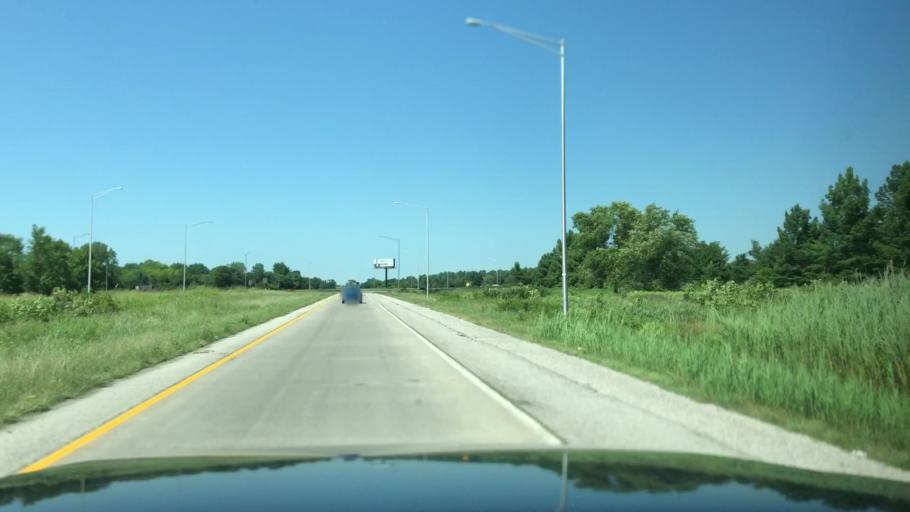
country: US
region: Illinois
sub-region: Saint Clair County
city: Alorton
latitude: 38.5813
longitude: -90.1050
